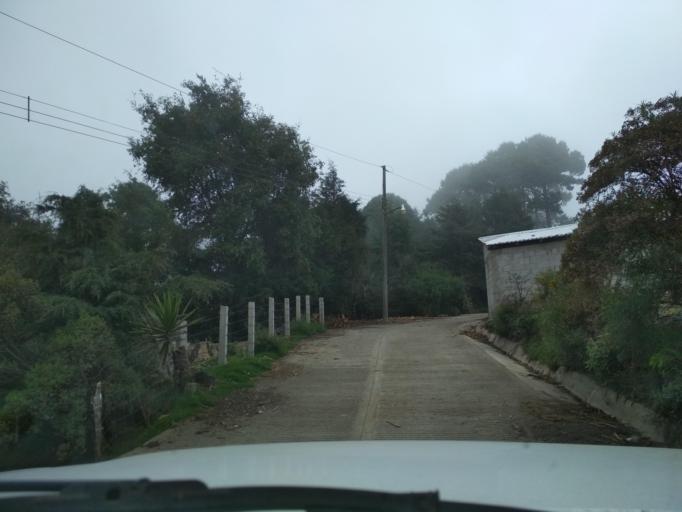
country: MX
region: Veracruz
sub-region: Mariano Escobedo
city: San Isidro el Berro
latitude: 18.9293
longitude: -97.2171
